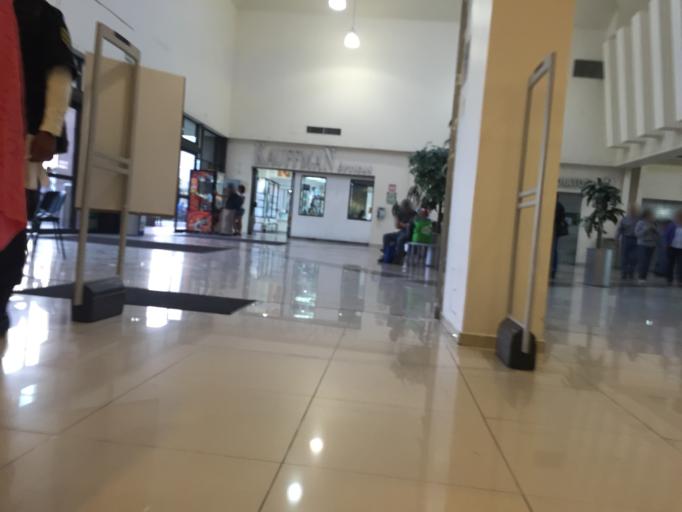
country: MX
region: Mexico City
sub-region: Iztacalco
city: Iztacalco
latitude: 19.3842
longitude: -99.0780
